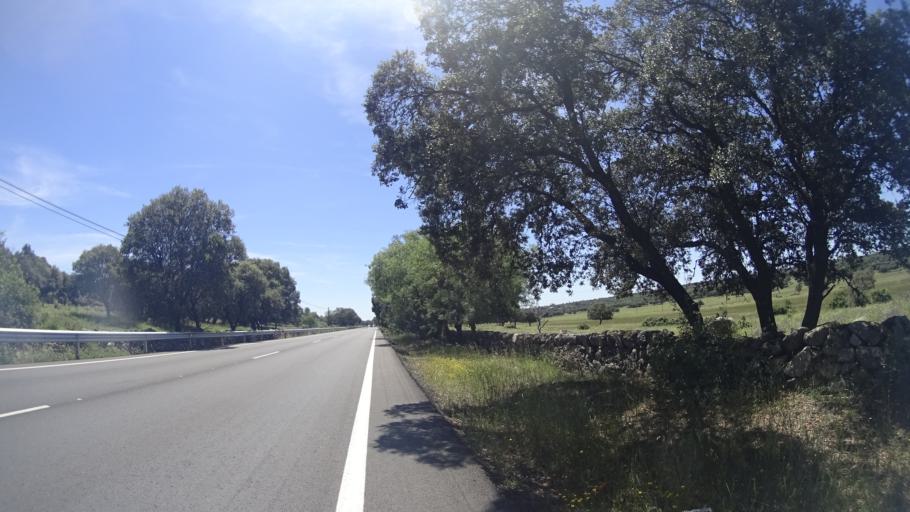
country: ES
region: Madrid
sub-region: Provincia de Madrid
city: Galapagar
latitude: 40.5982
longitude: -4.0177
